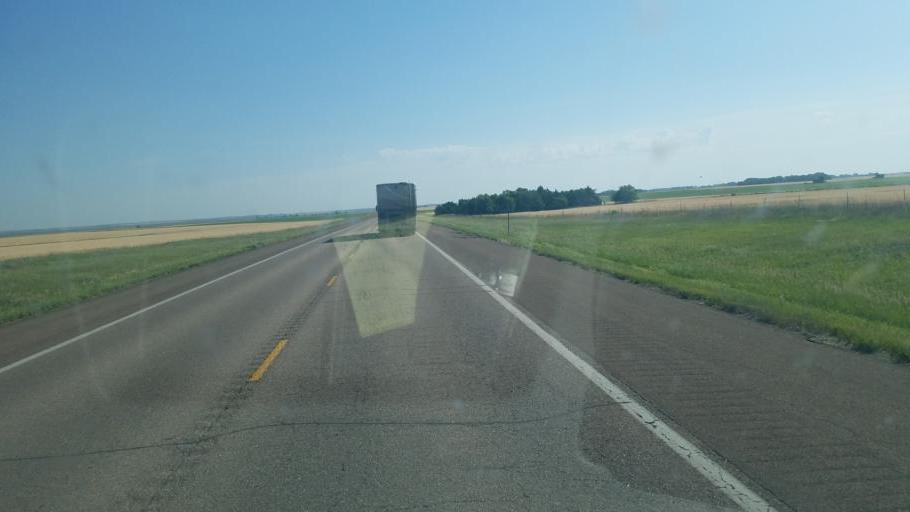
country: US
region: Kansas
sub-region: Barton County
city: Ellinwood
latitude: 38.4094
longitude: -98.6619
